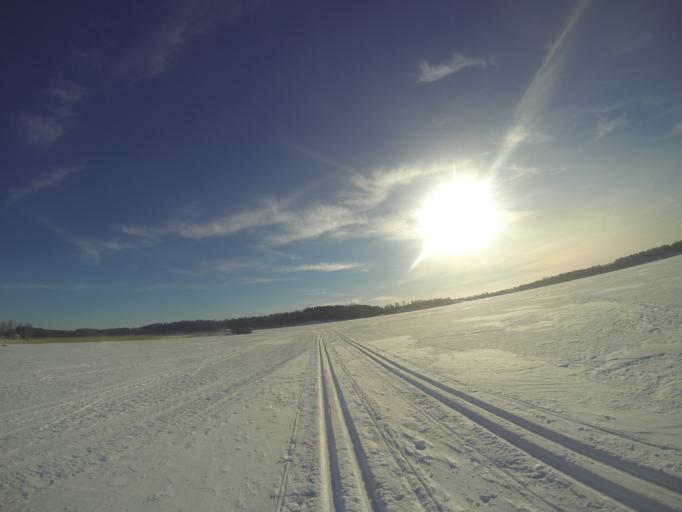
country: FI
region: Southern Savonia
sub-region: Savonlinna
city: Savonlinna
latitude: 61.8837
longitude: 28.9064
